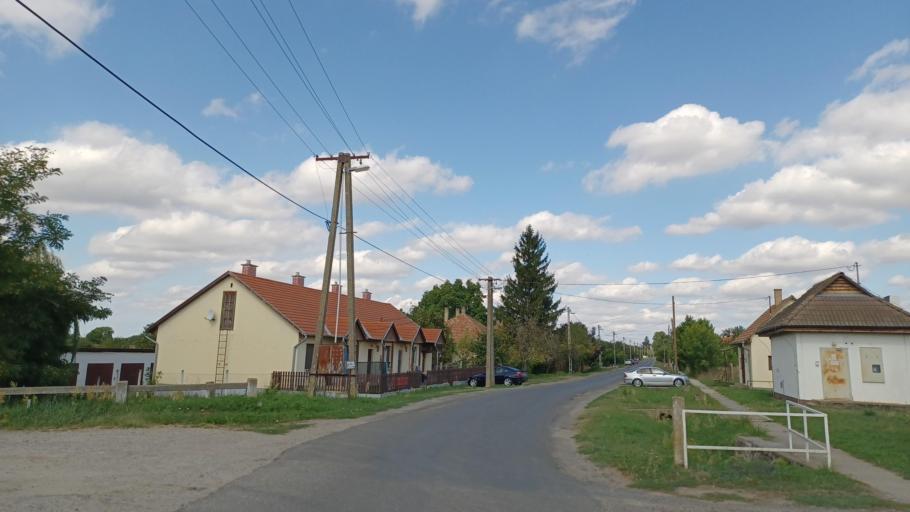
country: HU
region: Tolna
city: Pincehely
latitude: 46.7193
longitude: 18.4745
